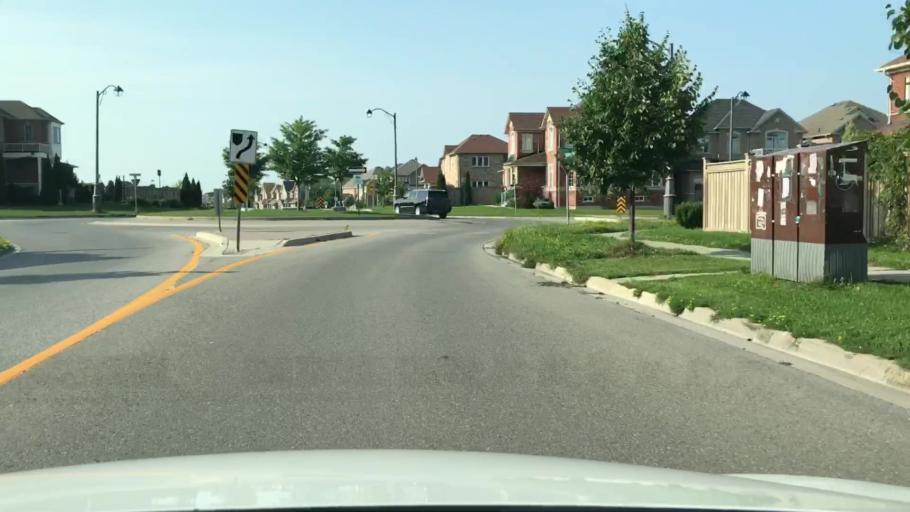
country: CA
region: Ontario
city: Newmarket
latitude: 44.0135
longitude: -79.4365
